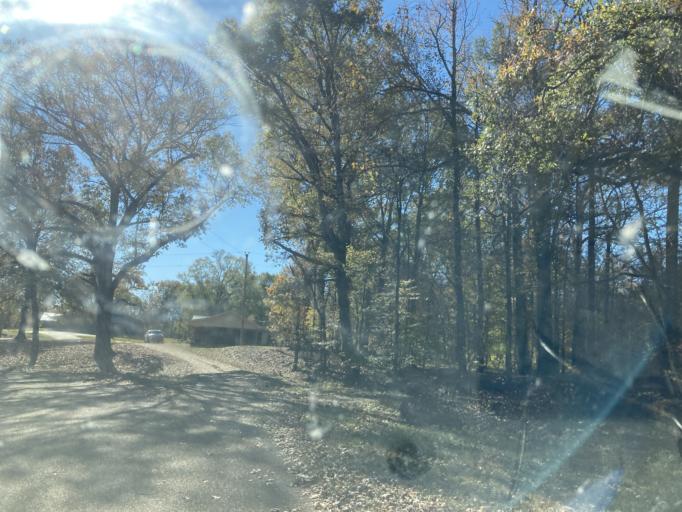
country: US
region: Mississippi
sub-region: Hinds County
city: Lynchburg
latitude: 32.5701
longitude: -90.5109
